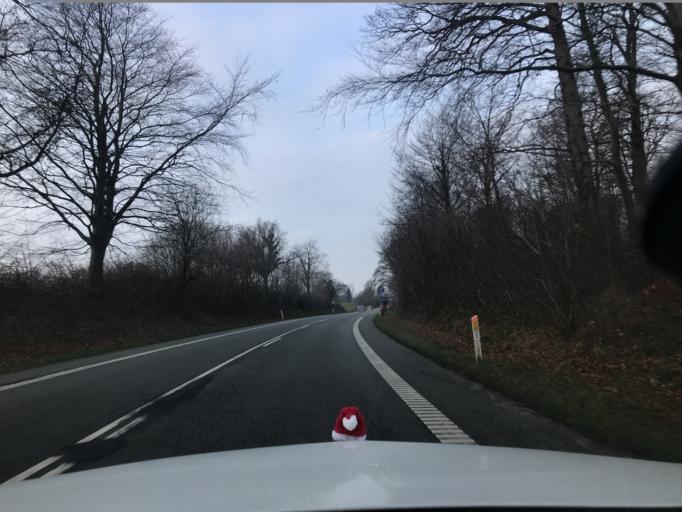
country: DK
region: South Denmark
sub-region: Sonderborg Kommune
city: Grasten
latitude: 54.9290
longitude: 9.5885
